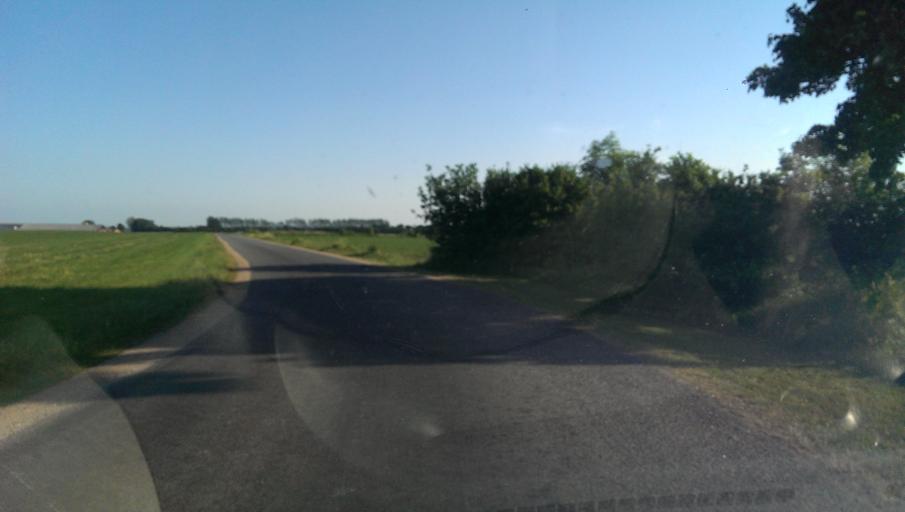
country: DK
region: South Denmark
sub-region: Esbjerg Kommune
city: Bramming
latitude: 55.5473
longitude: 8.6565
